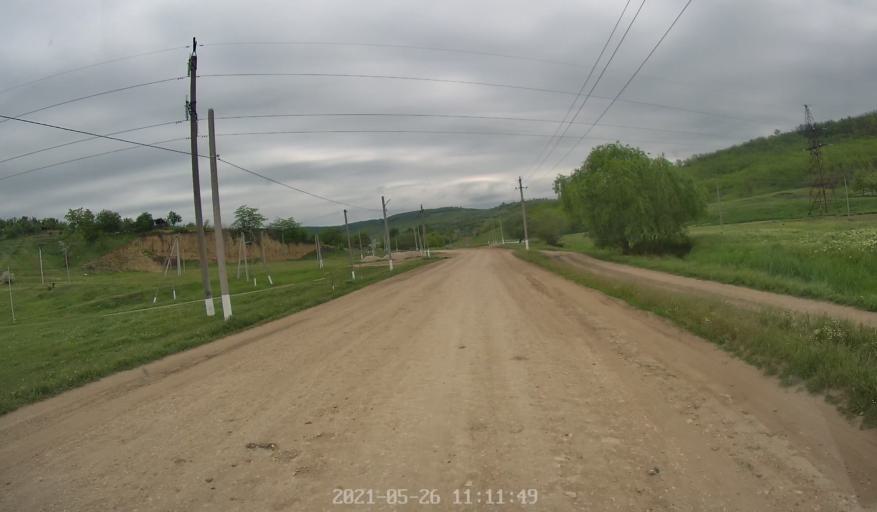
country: MD
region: Hincesti
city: Dancu
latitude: 46.8234
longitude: 28.3781
